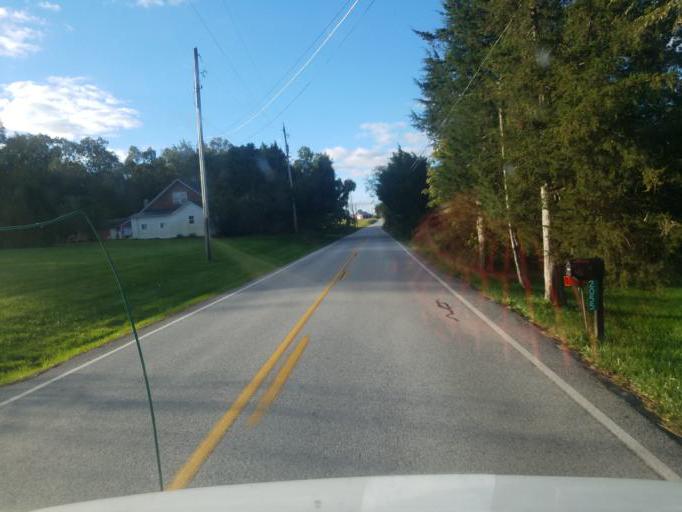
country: US
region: Pennsylvania
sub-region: Adams County
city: Biglerville
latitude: 39.9049
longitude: -77.2259
